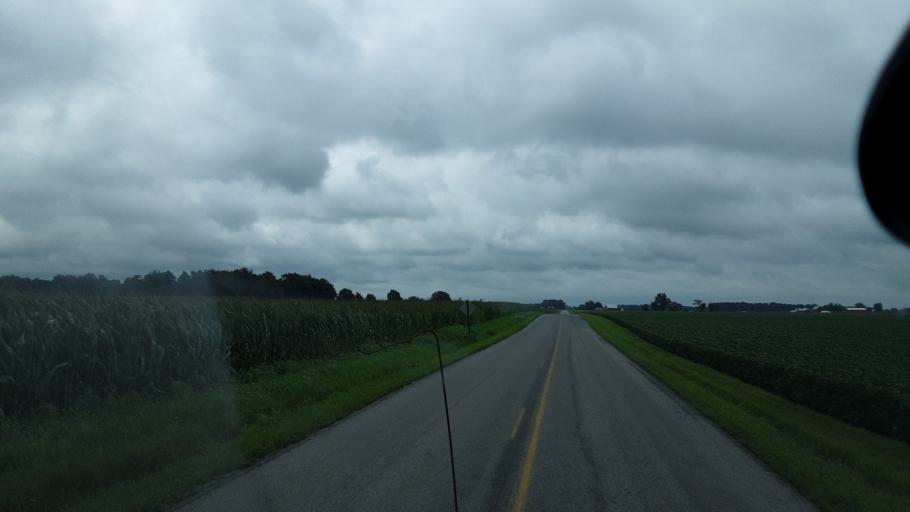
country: US
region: Indiana
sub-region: Wells County
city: Ossian
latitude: 40.8870
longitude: -85.1093
